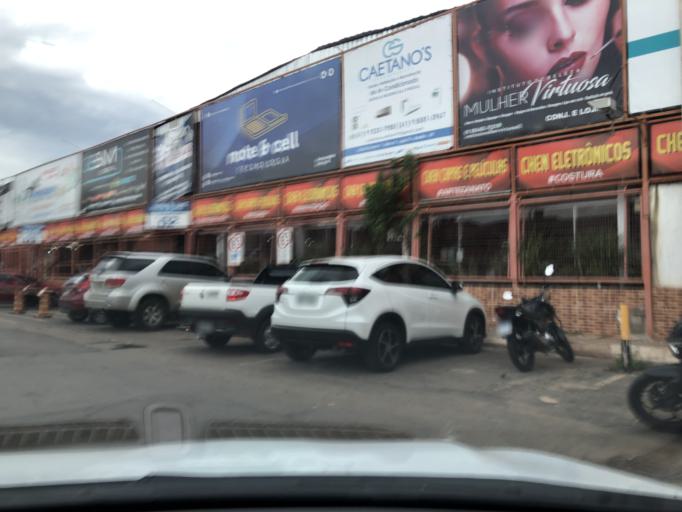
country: BR
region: Federal District
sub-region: Brasilia
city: Brasilia
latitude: -15.7952
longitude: -47.9515
